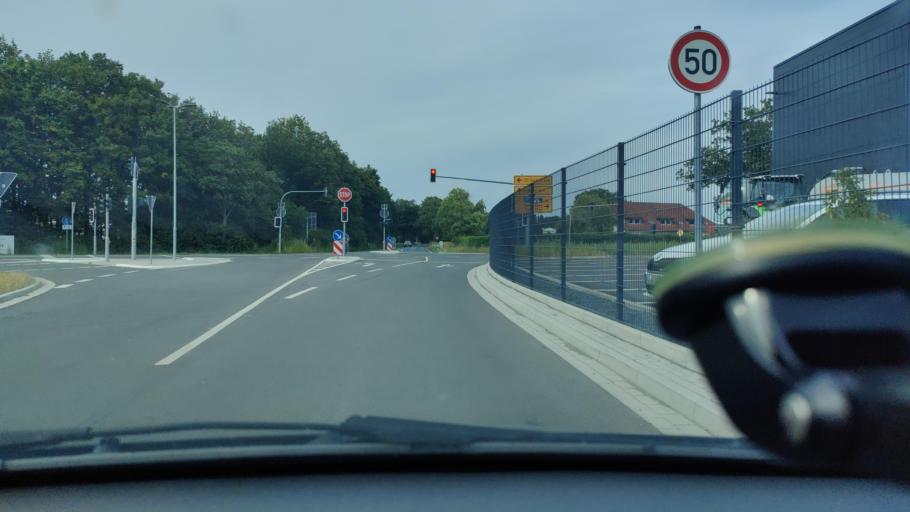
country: DE
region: North Rhine-Westphalia
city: Geldern
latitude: 51.5240
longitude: 6.3580
